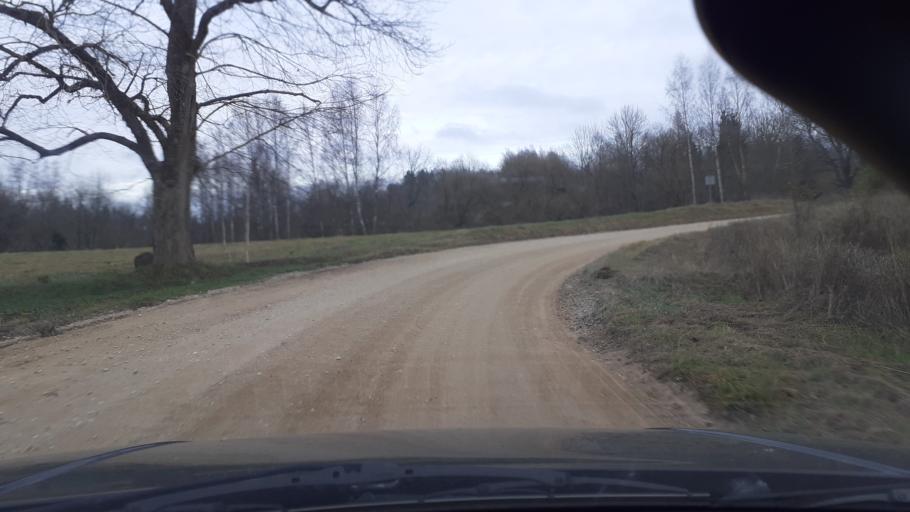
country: LV
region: Alsunga
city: Alsunga
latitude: 56.9461
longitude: 21.6372
